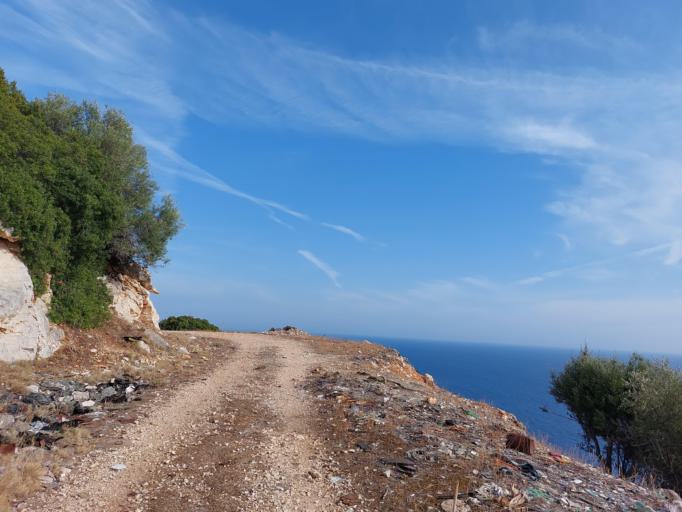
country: HR
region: Dubrovacko-Neretvanska
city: Smokvica
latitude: 42.7327
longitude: 16.8301
